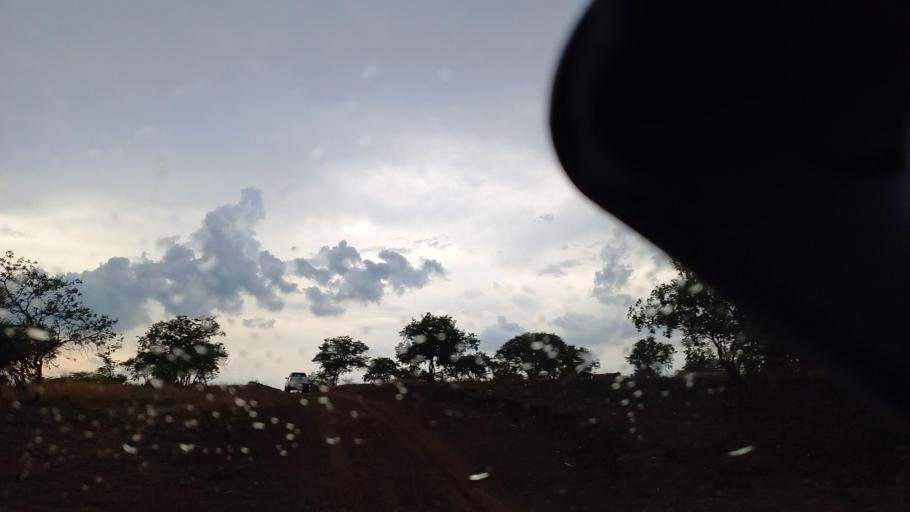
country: ZM
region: Lusaka
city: Kafue
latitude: -15.9736
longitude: 28.2521
